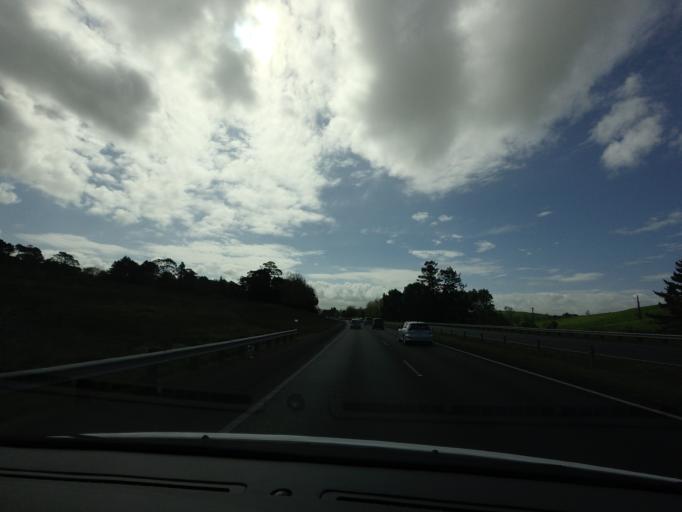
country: NZ
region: Auckland
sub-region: Auckland
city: Rothesay Bay
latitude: -36.6696
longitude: 174.6807
